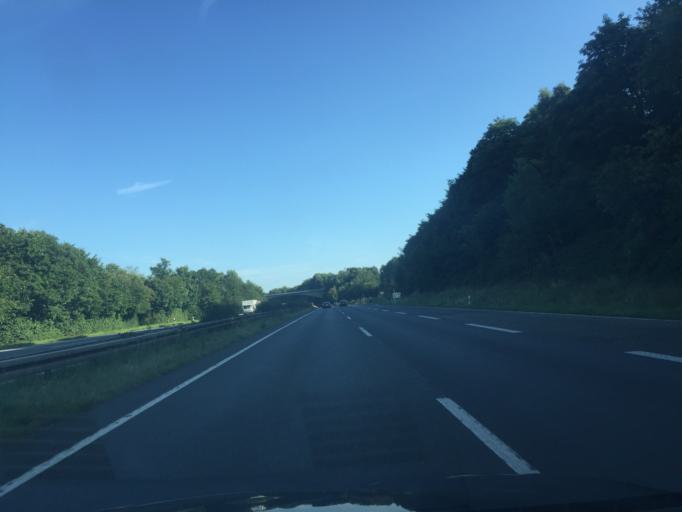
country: DE
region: North Rhine-Westphalia
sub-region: Regierungsbezirk Arnsberg
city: Nachrodt-Wiblingwerde
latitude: 51.2685
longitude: 7.6014
